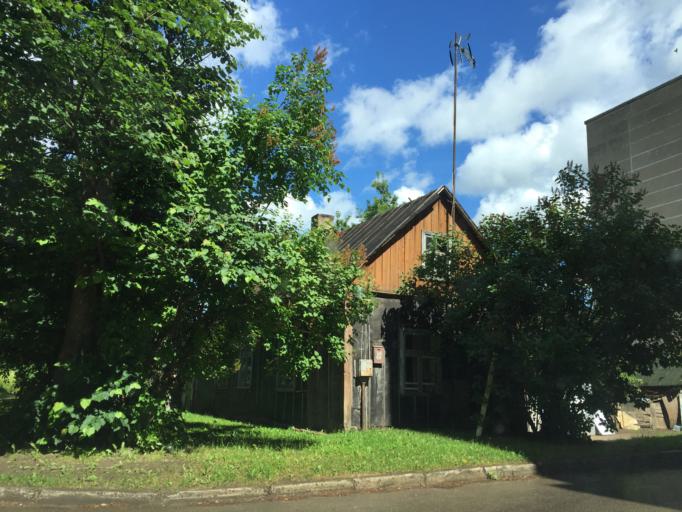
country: LV
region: Lecava
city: Iecava
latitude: 56.5970
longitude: 24.1920
